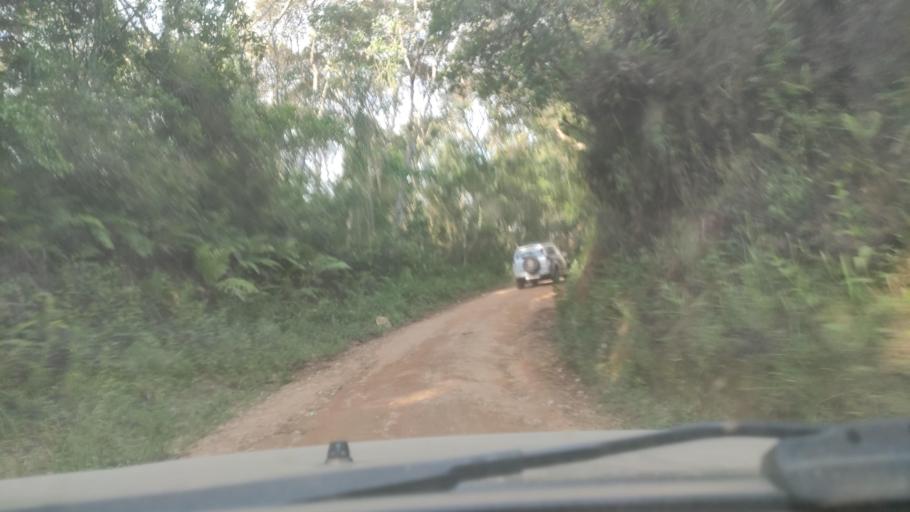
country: BR
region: Minas Gerais
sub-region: Cambui
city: Cambui
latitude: -22.7615
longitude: -45.9590
